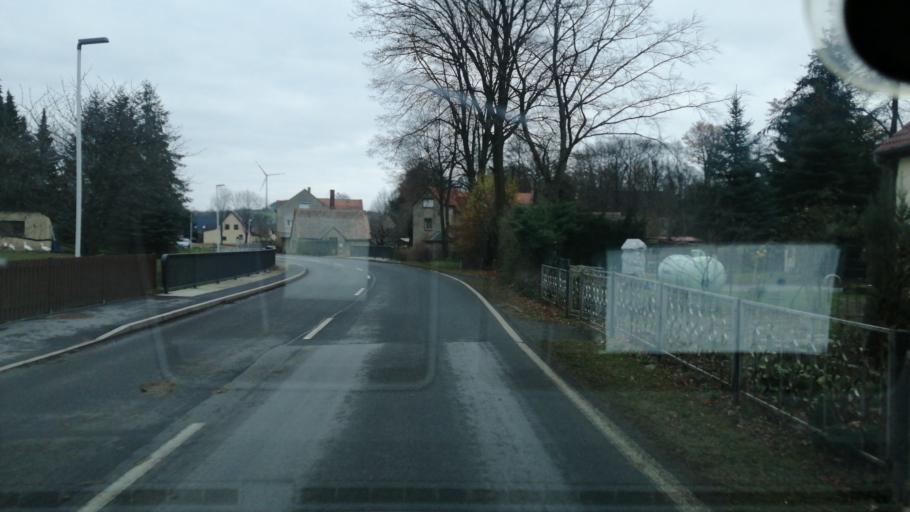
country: DE
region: Saxony
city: Bernstadt
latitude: 51.0669
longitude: 14.7864
